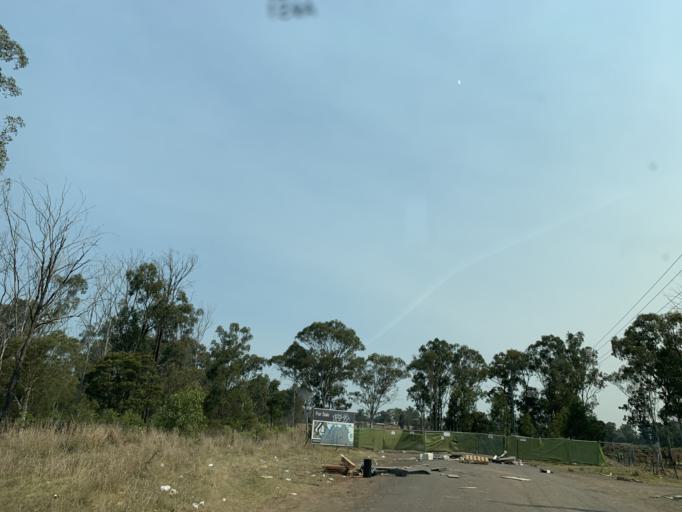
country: AU
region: New South Wales
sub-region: Blacktown
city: Blackett
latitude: -33.7195
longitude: 150.8196
